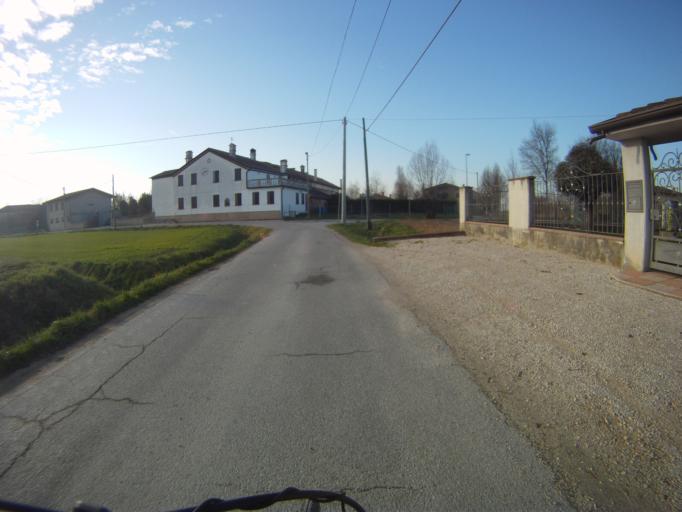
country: IT
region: Veneto
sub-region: Provincia di Padova
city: Polverara
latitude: 45.3125
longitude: 11.9501
